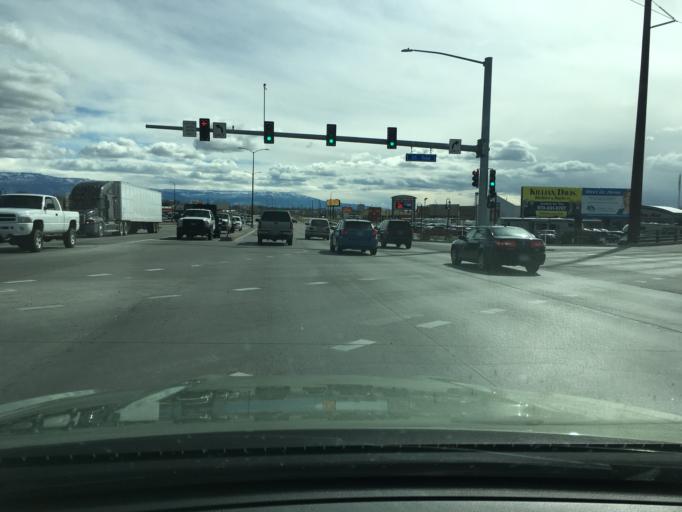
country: US
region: Colorado
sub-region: Mesa County
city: Grand Junction
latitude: 39.0831
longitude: -108.5895
